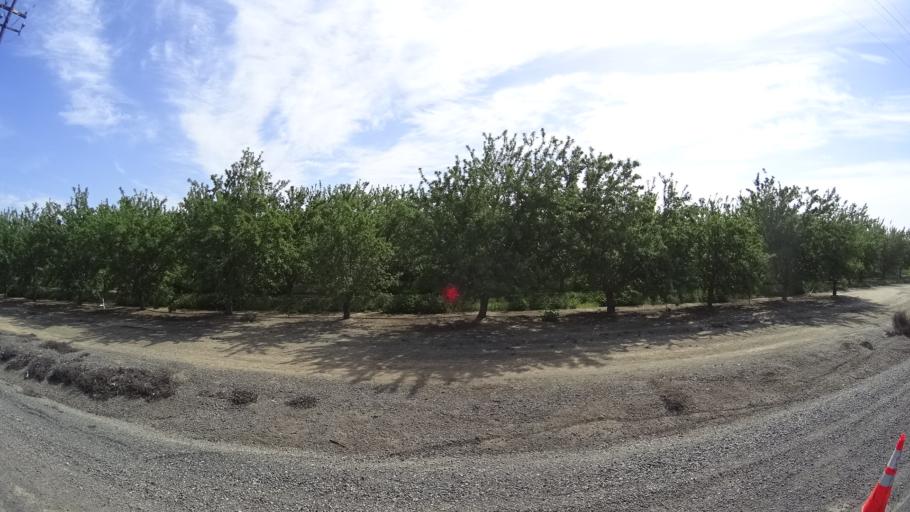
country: US
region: California
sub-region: Glenn County
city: Hamilton City
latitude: 39.6475
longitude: -122.0077
